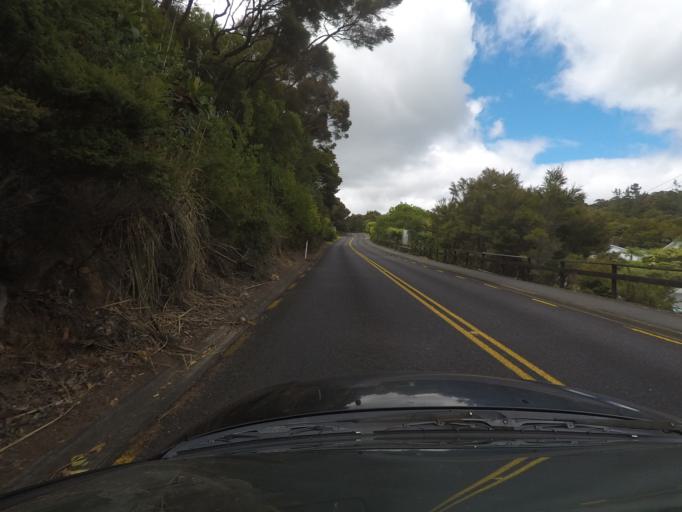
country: NZ
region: Northland
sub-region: Far North District
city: Paihia
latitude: -35.2874
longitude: 174.0962
